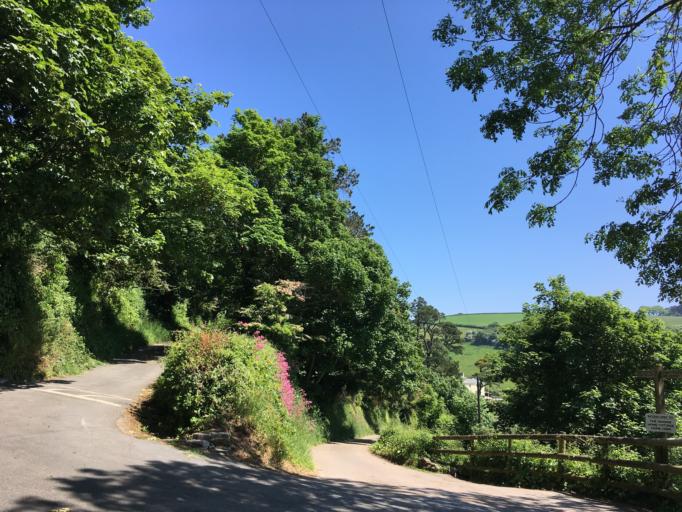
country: GB
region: England
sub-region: Devon
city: Dartmouth
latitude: 50.3453
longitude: -3.5565
